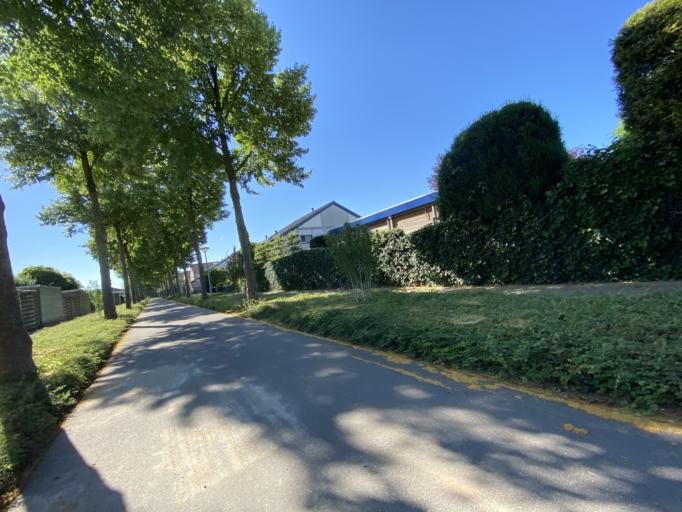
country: NL
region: Gelderland
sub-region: Gemeente Duiven
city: Duiven
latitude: 51.9449
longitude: 5.9965
